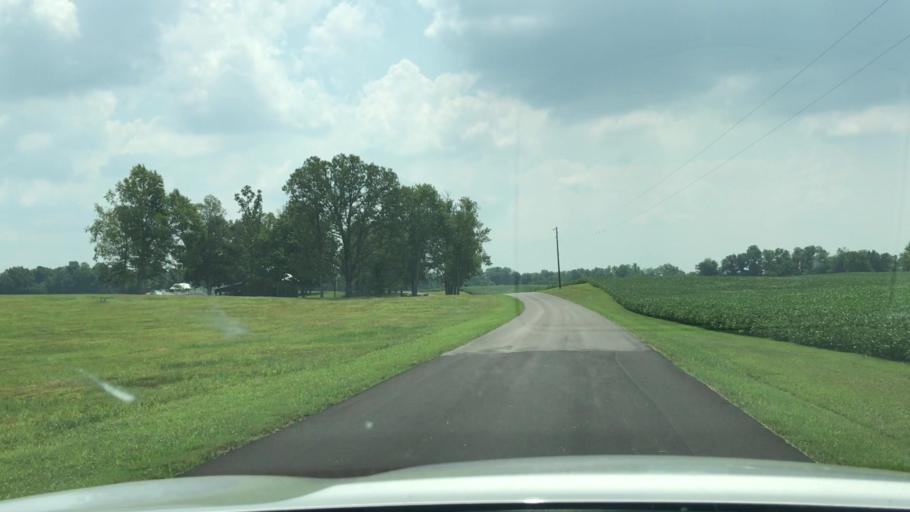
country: US
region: Kentucky
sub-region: Todd County
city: Elkton
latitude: 36.7695
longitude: -87.1409
